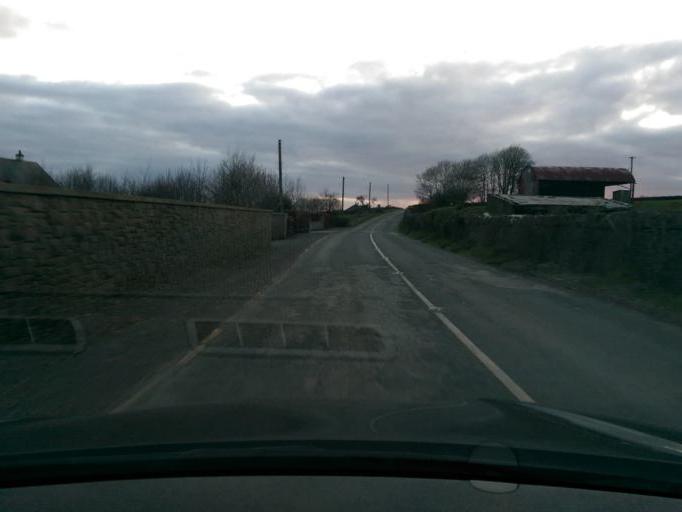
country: IE
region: Connaught
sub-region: County Galway
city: Portumna
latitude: 53.0995
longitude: -8.1517
